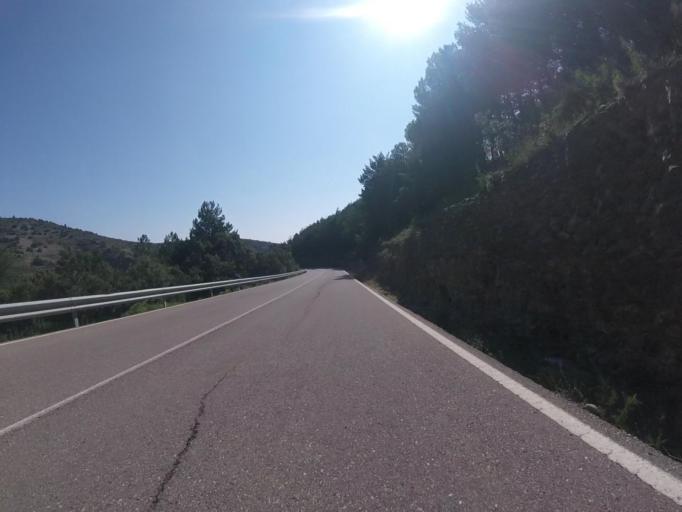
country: ES
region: Valencia
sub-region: Provincia de Castello
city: Benafigos
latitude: 40.2678
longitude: -0.2400
